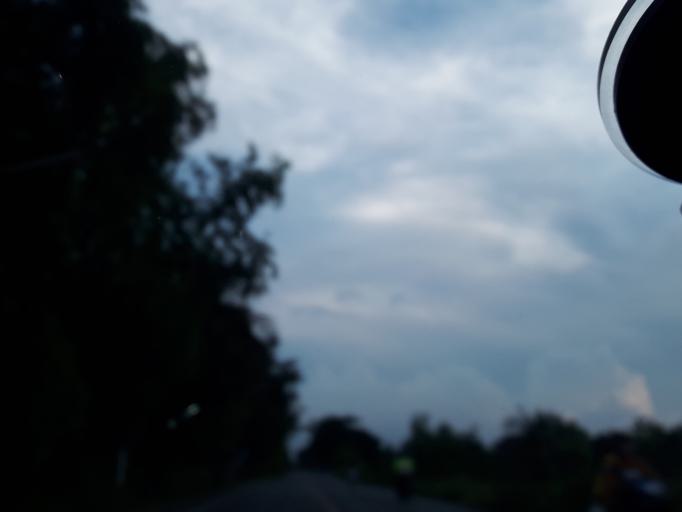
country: TH
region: Pathum Thani
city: Nong Suea
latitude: 14.1318
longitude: 100.8690
